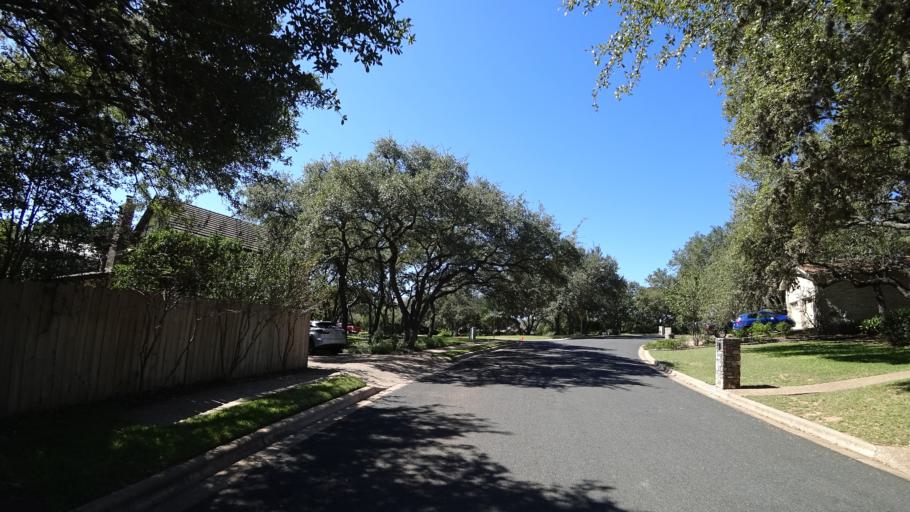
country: US
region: Texas
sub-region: Travis County
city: West Lake Hills
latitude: 30.3407
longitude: -97.7833
